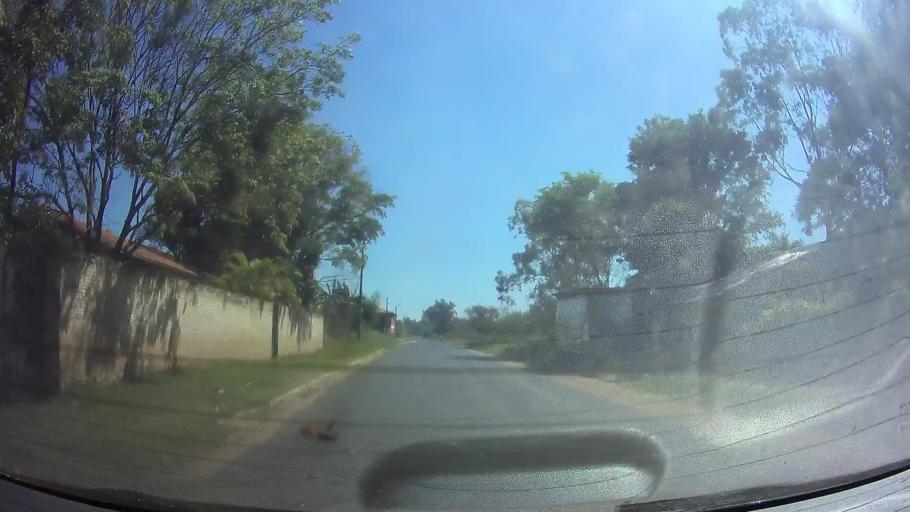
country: PY
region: Central
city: Fernando de la Mora
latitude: -25.2852
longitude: -57.5419
